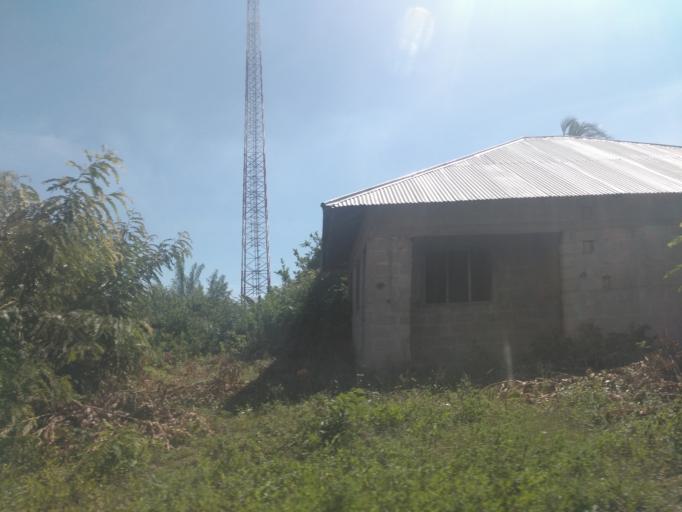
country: TZ
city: Kiwengwa
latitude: -5.9915
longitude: 39.3357
